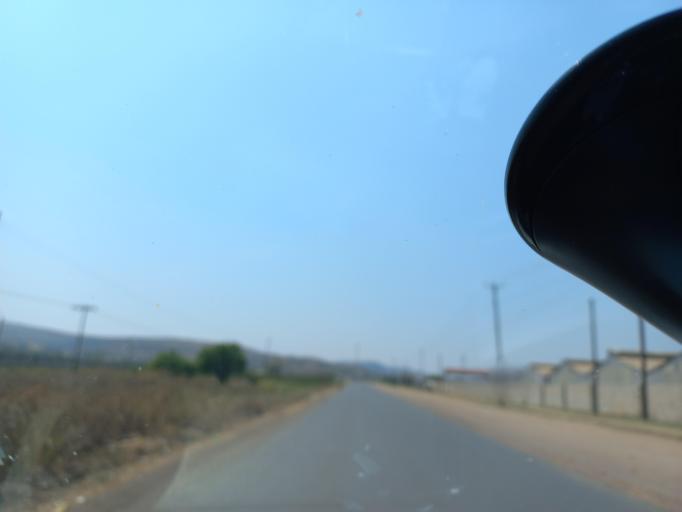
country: ZM
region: Lusaka
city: Kafue
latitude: -15.7565
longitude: 28.1711
